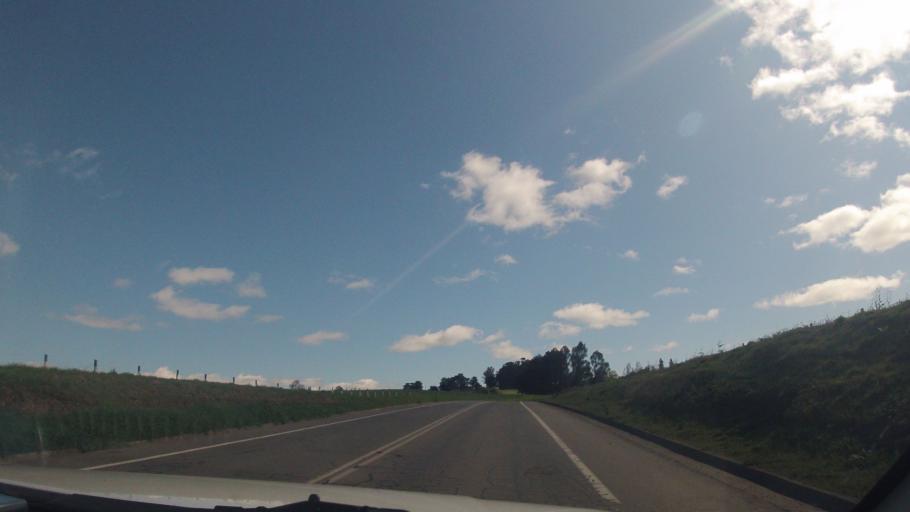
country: CL
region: Araucania
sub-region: Provincia de Malleco
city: Traiguen
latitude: -38.2200
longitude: -72.7129
